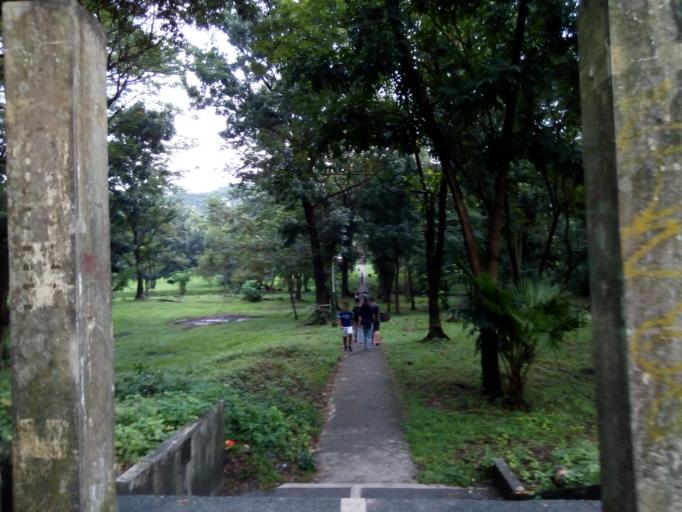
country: PH
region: Metro Manila
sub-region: Quezon City
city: Quezon City
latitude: 14.6542
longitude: 121.0698
